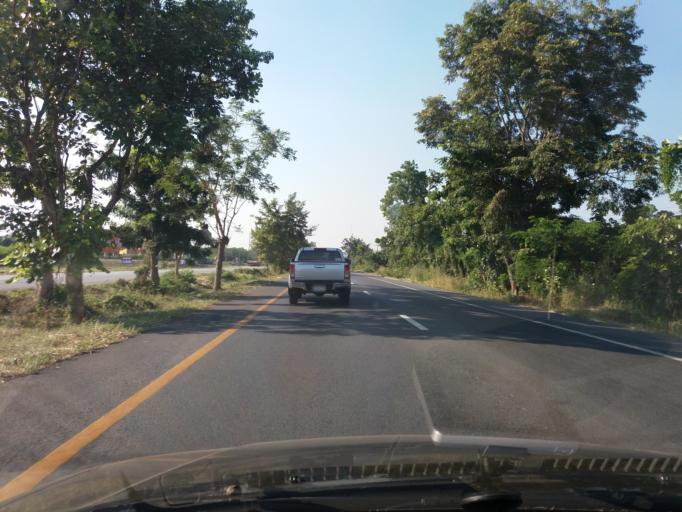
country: TH
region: Nakhon Sawan
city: Kao Liao
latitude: 15.7538
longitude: 100.0011
